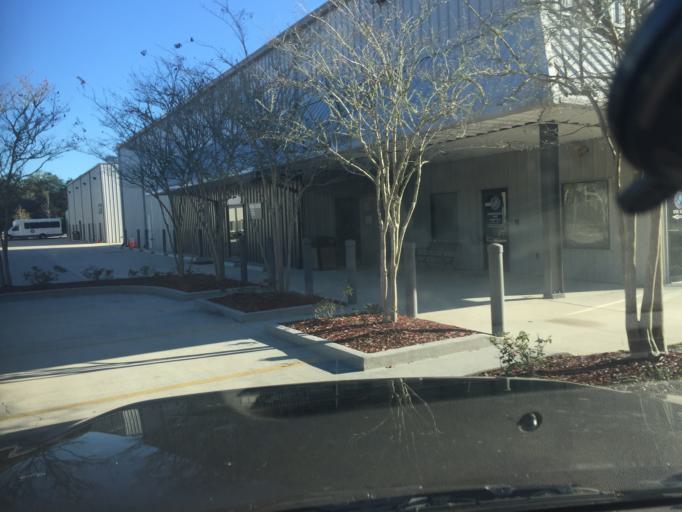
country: US
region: Louisiana
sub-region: Saint Tammany Parish
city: Slidell
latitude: 30.2433
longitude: -89.7585
